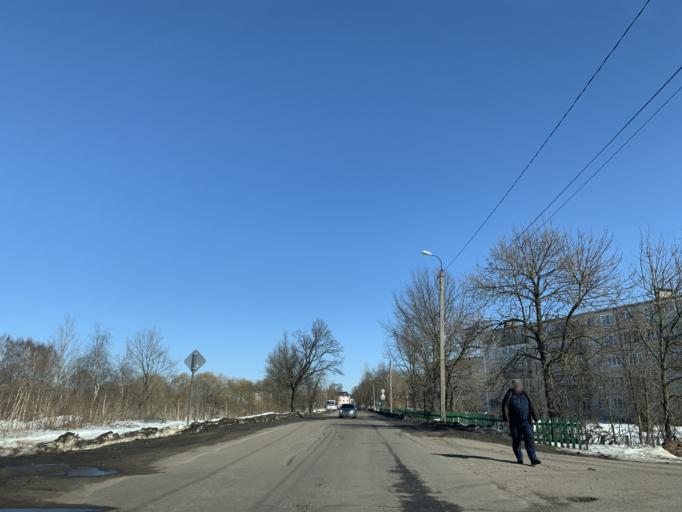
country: RU
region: Jaroslavl
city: Konstantinovskiy
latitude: 57.8402
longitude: 39.5721
